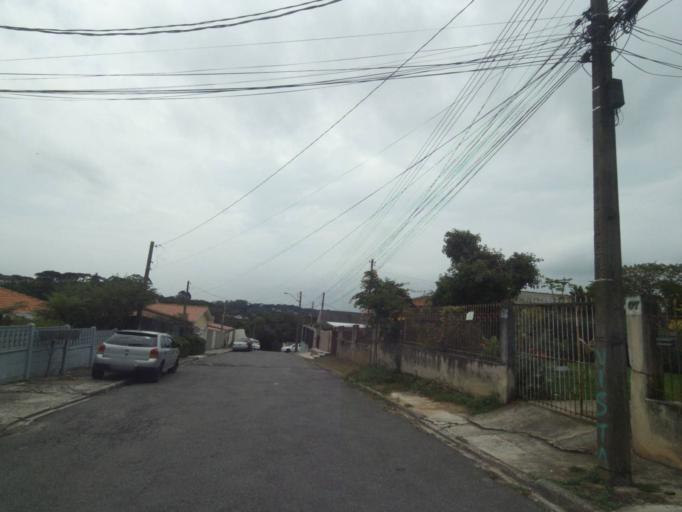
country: BR
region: Parana
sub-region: Curitiba
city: Curitiba
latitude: -25.4065
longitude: -49.2944
